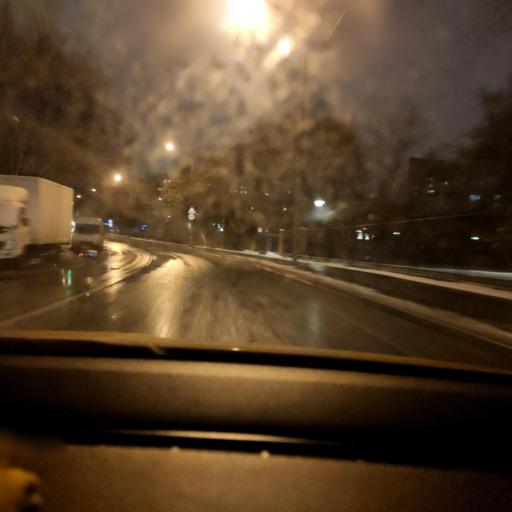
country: RU
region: Moscow
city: Leonovo
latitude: 55.8693
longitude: 37.6470
